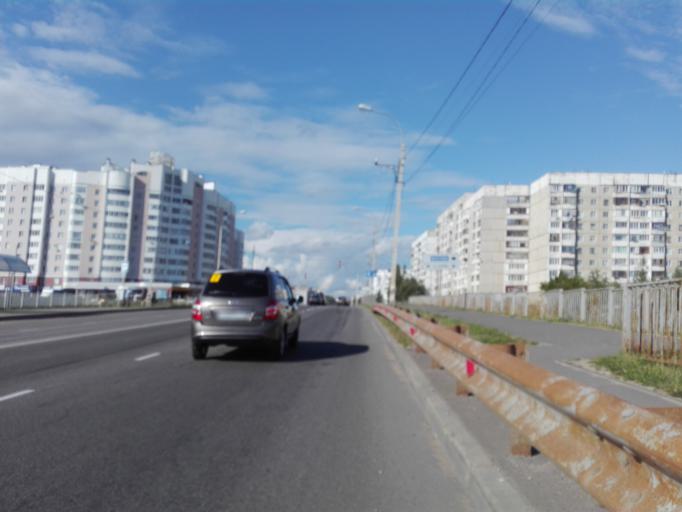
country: RU
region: Orjol
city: Orel
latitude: 53.0099
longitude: 36.1246
